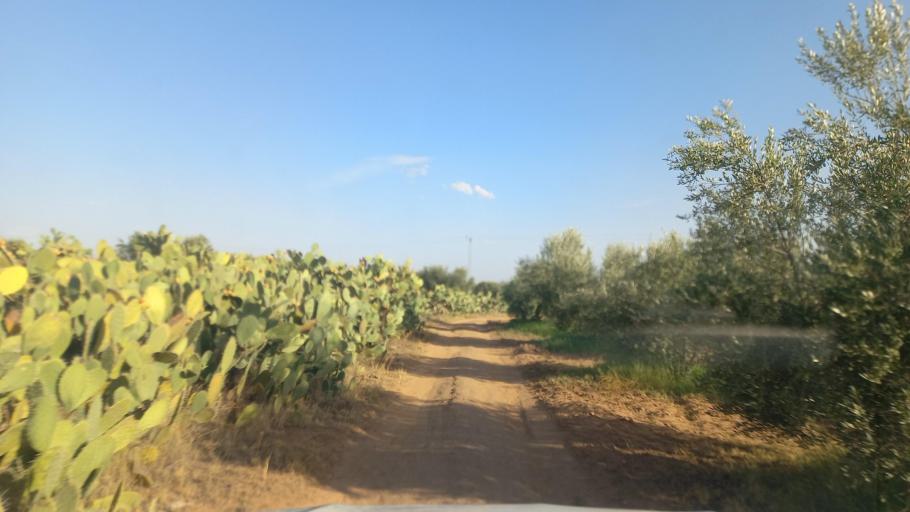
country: TN
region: Al Qasrayn
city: Kasserine
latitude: 35.2681
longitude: 9.0324
